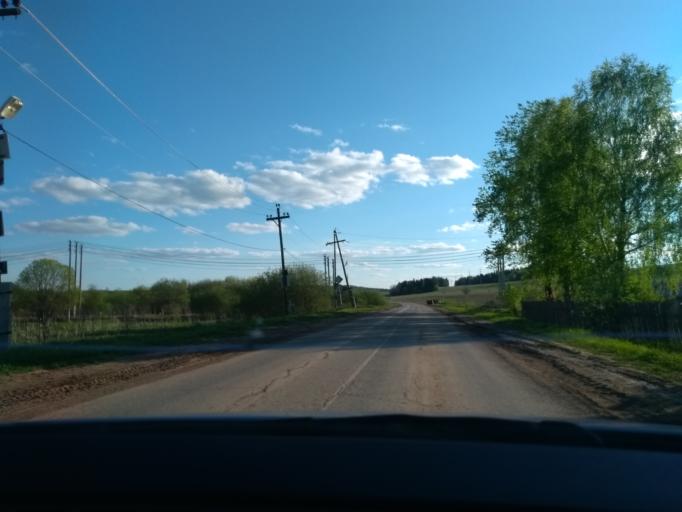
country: RU
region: Perm
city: Sylva
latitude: 57.8340
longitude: 56.6700
